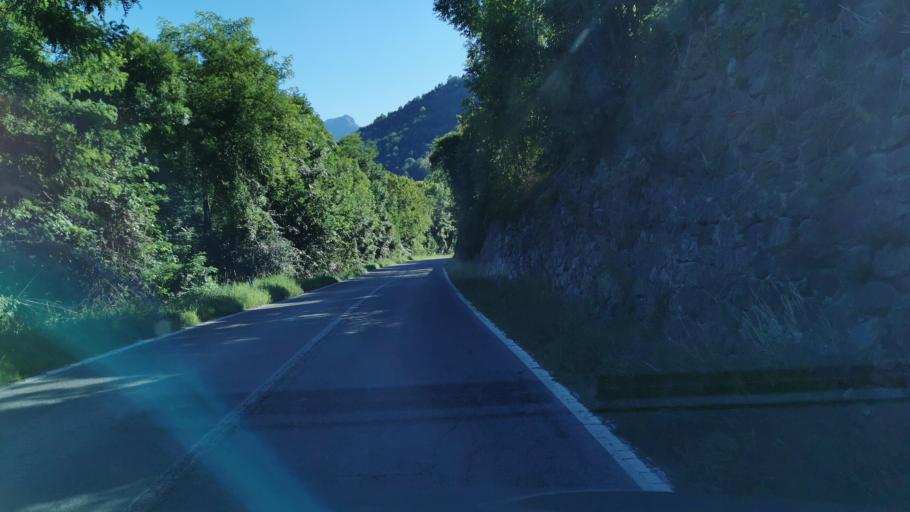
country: IT
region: Piedmont
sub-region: Provincia di Cuneo
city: Roccavione
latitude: 44.3091
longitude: 7.4555
